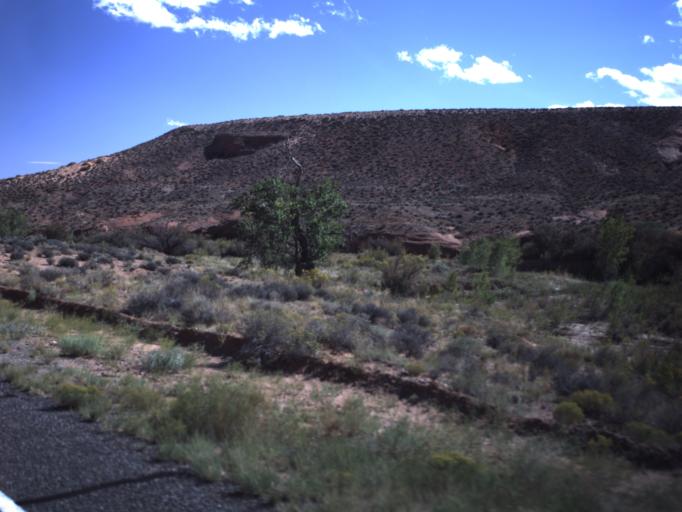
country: US
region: Utah
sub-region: Wayne County
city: Loa
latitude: 38.0565
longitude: -110.5917
